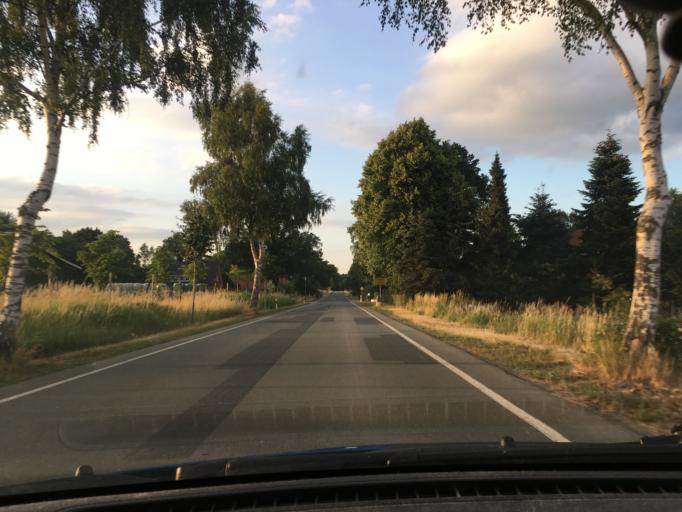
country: DE
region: Lower Saxony
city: Eyendorf
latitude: 53.1913
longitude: 10.1896
